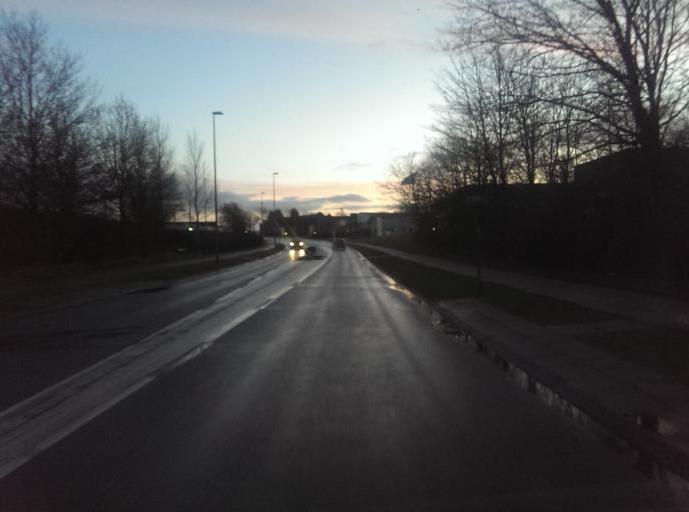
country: DK
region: South Denmark
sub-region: Esbjerg Kommune
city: Esbjerg
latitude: 55.4946
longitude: 8.4662
